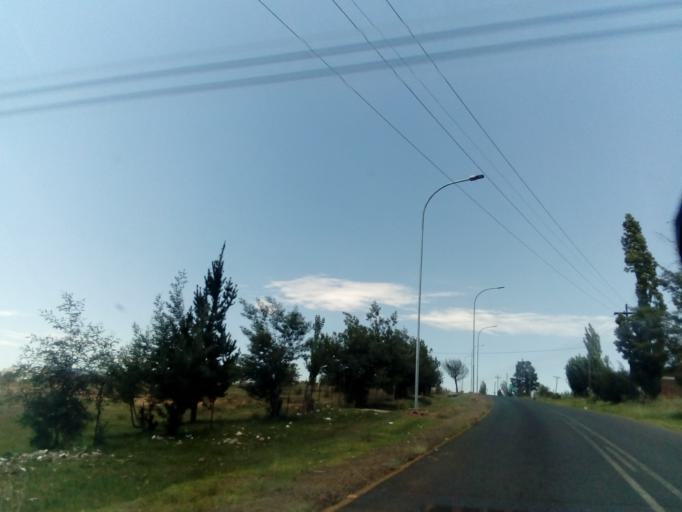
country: LS
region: Berea
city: Teyateyaneng
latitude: -29.1356
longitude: 27.7685
